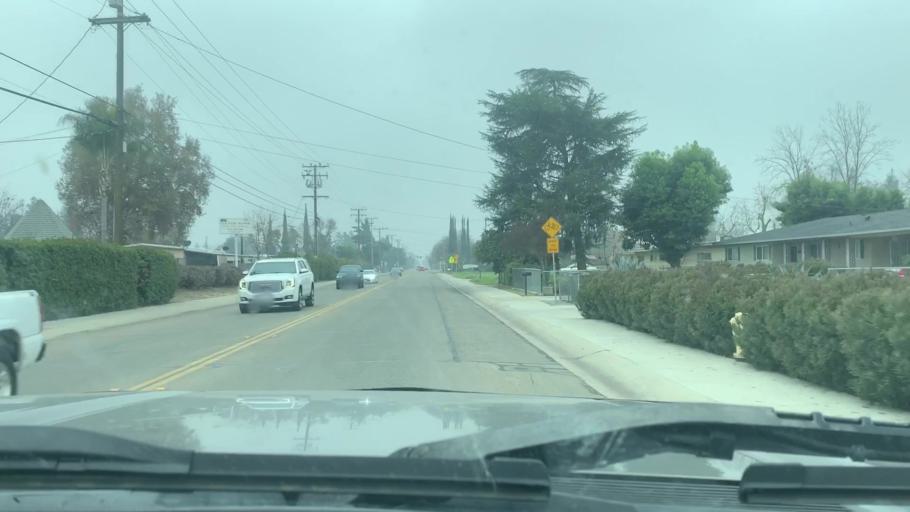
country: US
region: California
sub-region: Tulare County
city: Visalia
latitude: 36.3235
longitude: -119.3363
